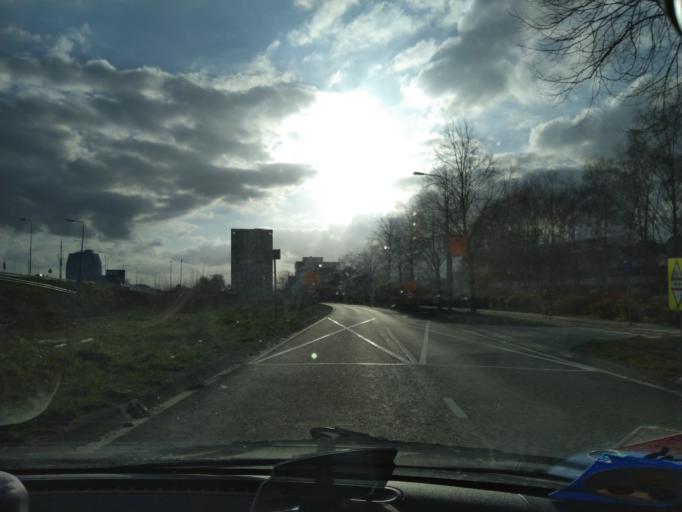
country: NL
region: Groningen
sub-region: Gemeente Groningen
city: Oosterpark
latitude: 53.2130
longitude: 6.5910
